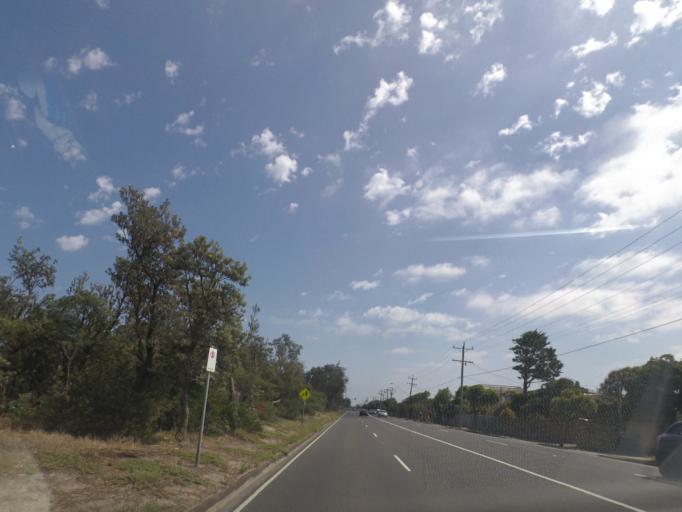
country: AU
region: Victoria
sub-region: Frankston
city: Seaford
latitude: -38.1120
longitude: 145.1256
